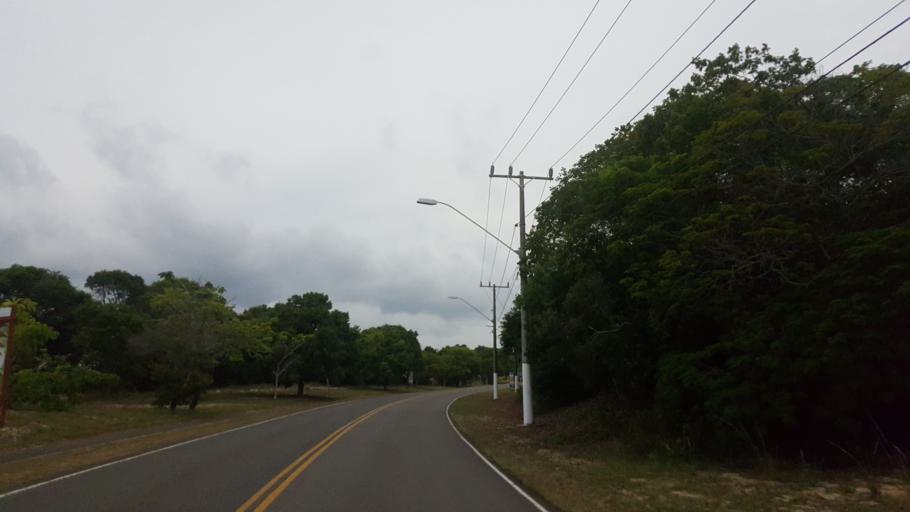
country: BR
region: Bahia
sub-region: Mata De Sao Joao
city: Mata de Sao Joao
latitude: -12.4272
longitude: -37.9220
